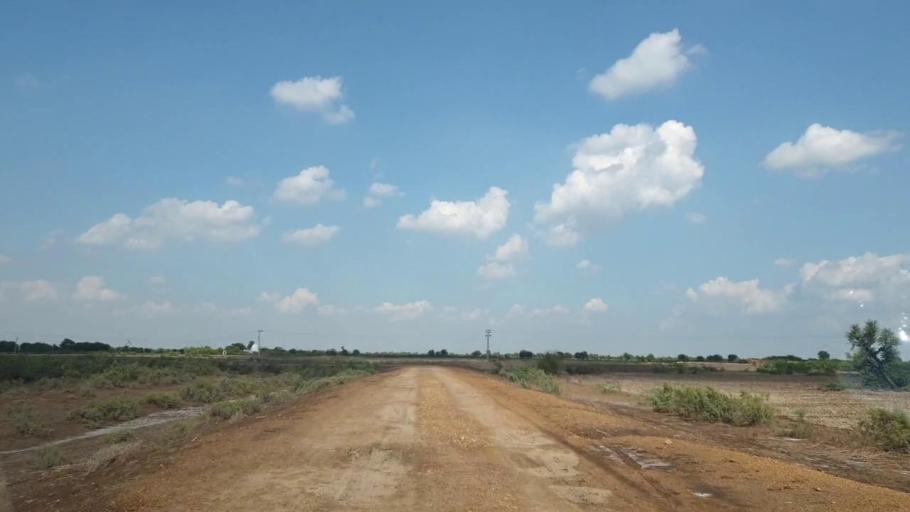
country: PK
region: Sindh
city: Pithoro
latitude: 25.6026
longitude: 69.3780
